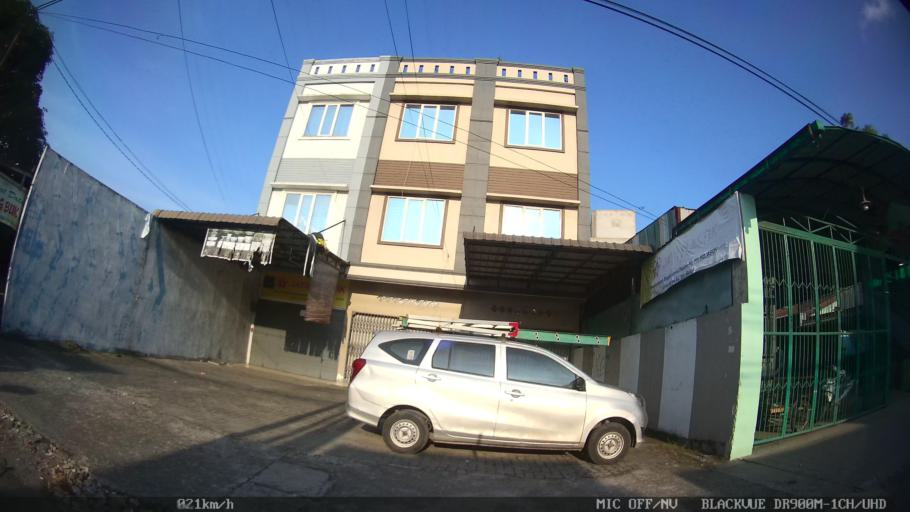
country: ID
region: North Sumatra
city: Medan
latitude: 3.6185
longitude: 98.6654
